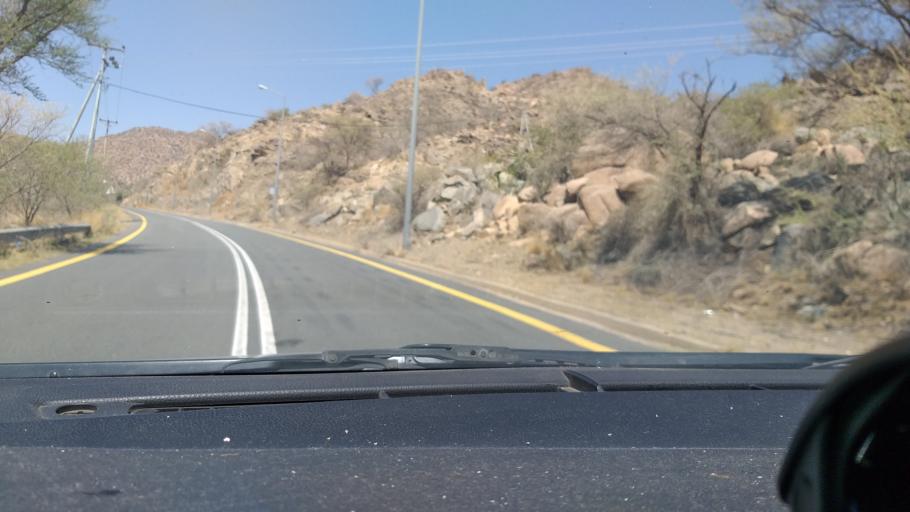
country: SA
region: Makkah
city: Ash Shafa
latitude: 21.0929
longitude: 40.3563
